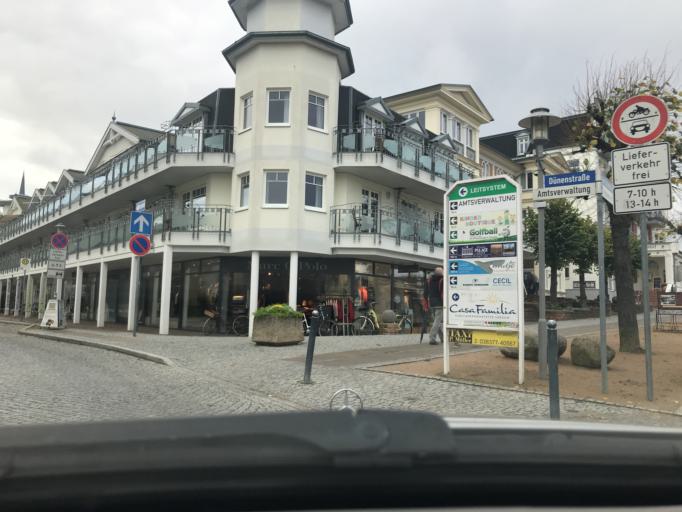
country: DE
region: Mecklenburg-Vorpommern
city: Ostseebad Zinnowitz
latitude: 54.0804
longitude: 13.9143
